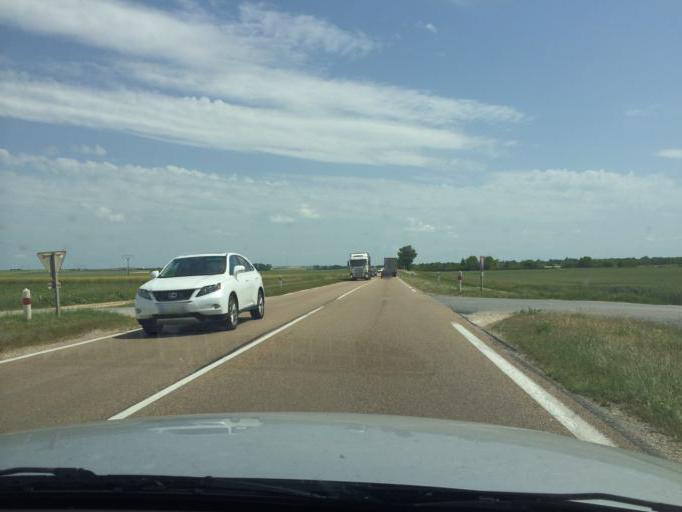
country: FR
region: Champagne-Ardenne
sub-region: Departement de la Marne
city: Sarry
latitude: 48.9218
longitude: 4.4172
